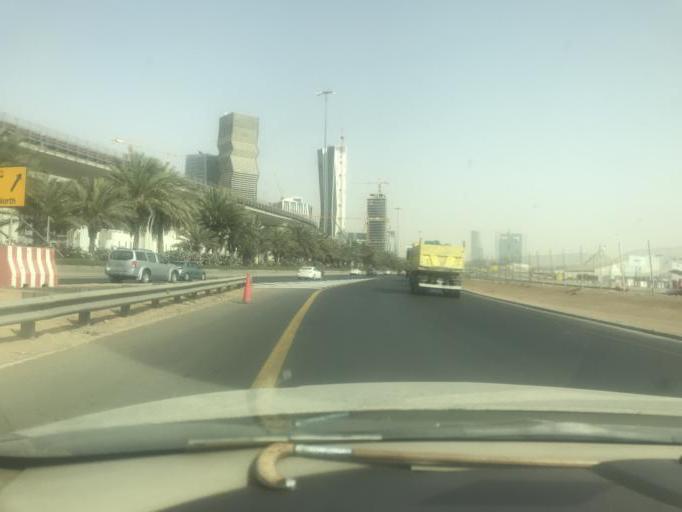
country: SA
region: Ar Riyad
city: Riyadh
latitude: 24.7644
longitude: 46.6459
